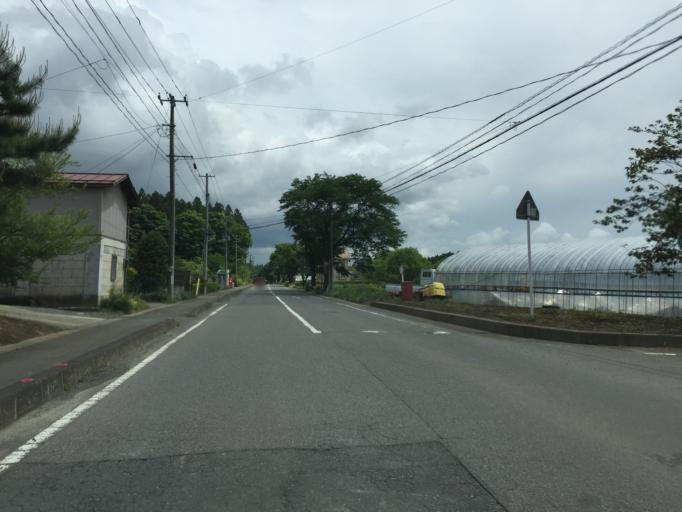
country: JP
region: Fukushima
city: Ishikawa
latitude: 37.1128
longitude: 140.3277
